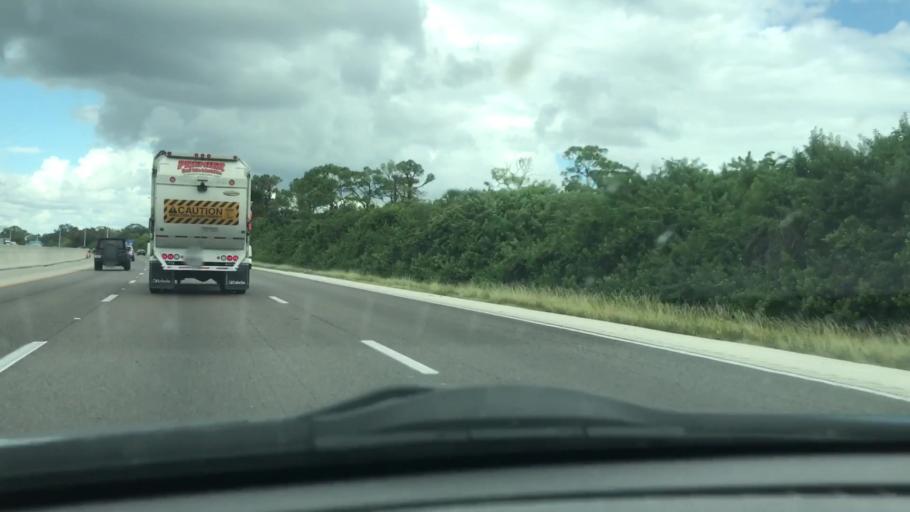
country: US
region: Florida
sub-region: Brevard County
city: Rockledge
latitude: 28.2826
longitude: -80.7336
